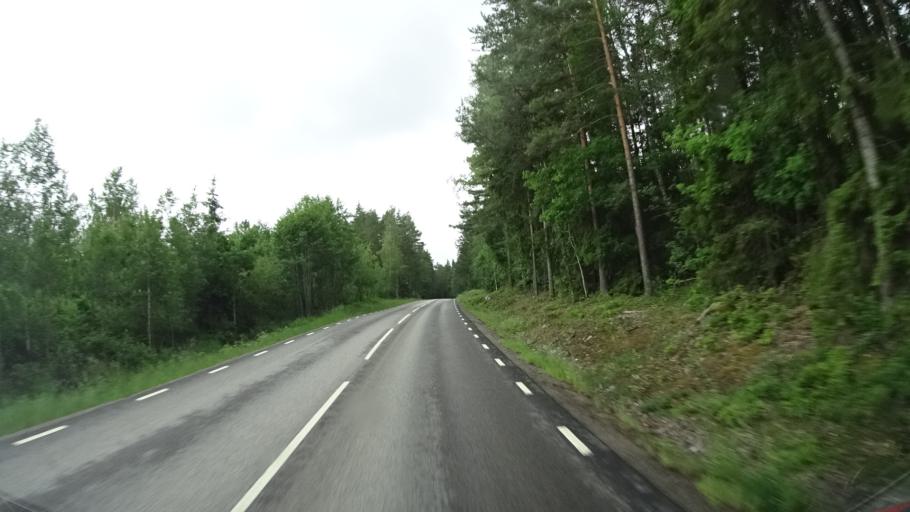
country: SE
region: Kalmar
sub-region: Oskarshamns Kommun
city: Oskarshamn
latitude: 57.3808
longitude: 16.2229
